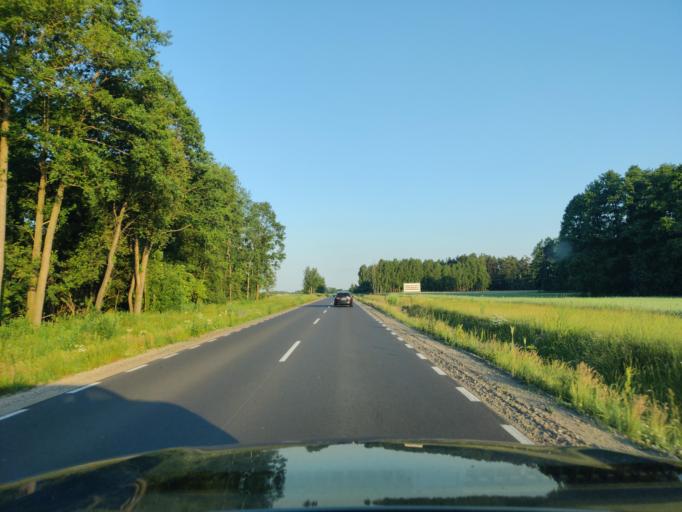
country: PL
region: Masovian Voivodeship
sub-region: Powiat plonski
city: Baboszewo
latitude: 52.7158
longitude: 20.3310
